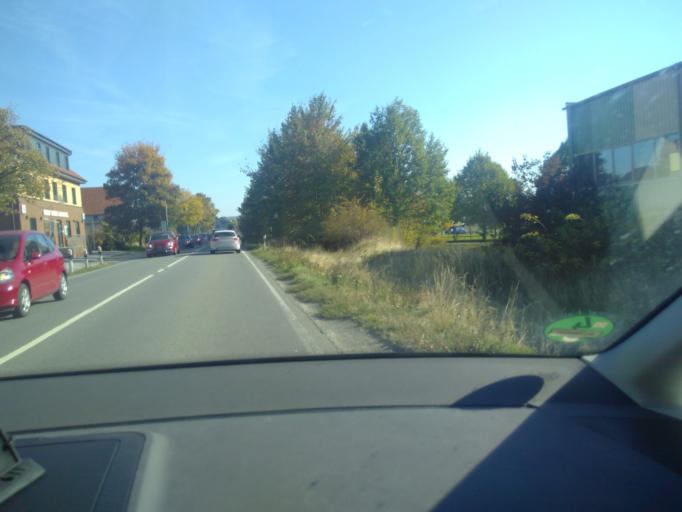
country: DE
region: North Rhine-Westphalia
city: Halle
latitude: 52.0686
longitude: 8.3434
